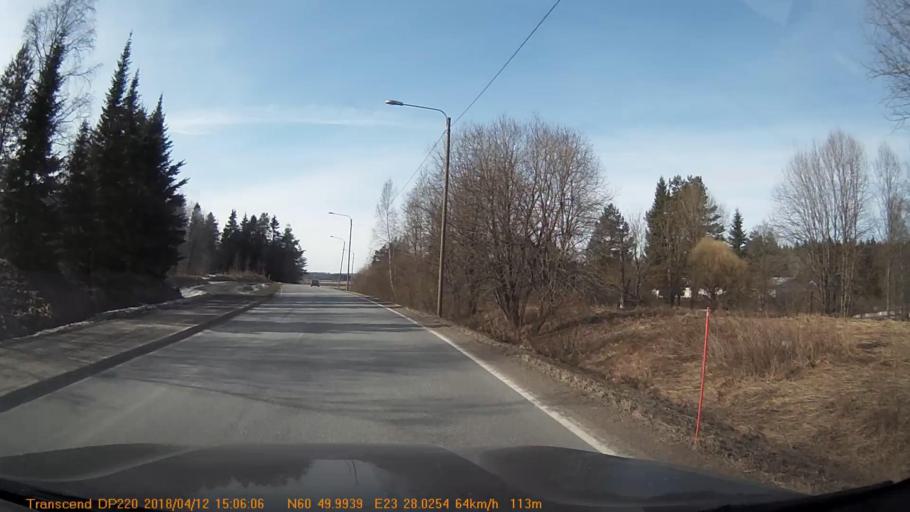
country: FI
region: Haeme
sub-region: Forssa
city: Jokioinen
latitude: 60.8334
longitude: 23.4668
